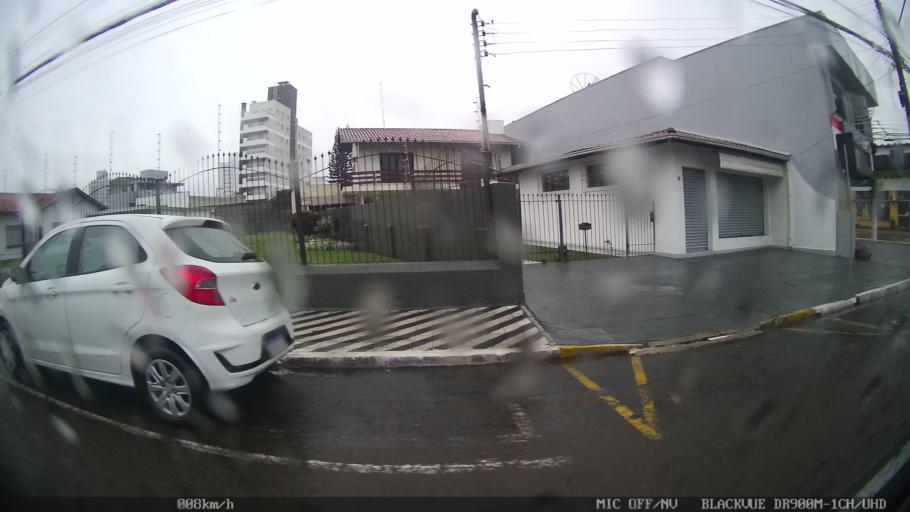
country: BR
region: Santa Catarina
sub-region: Itajai
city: Itajai
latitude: -26.9032
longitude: -48.6694
